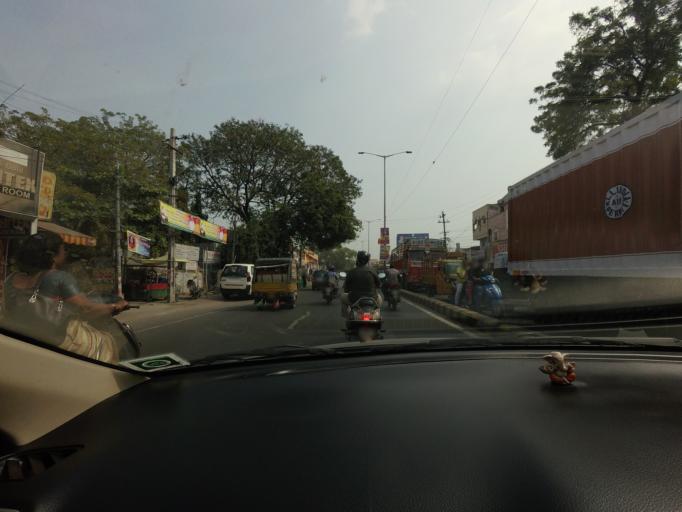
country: IN
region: Andhra Pradesh
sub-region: Krishna
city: Yanamalakuduru
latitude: 16.4952
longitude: 80.6609
